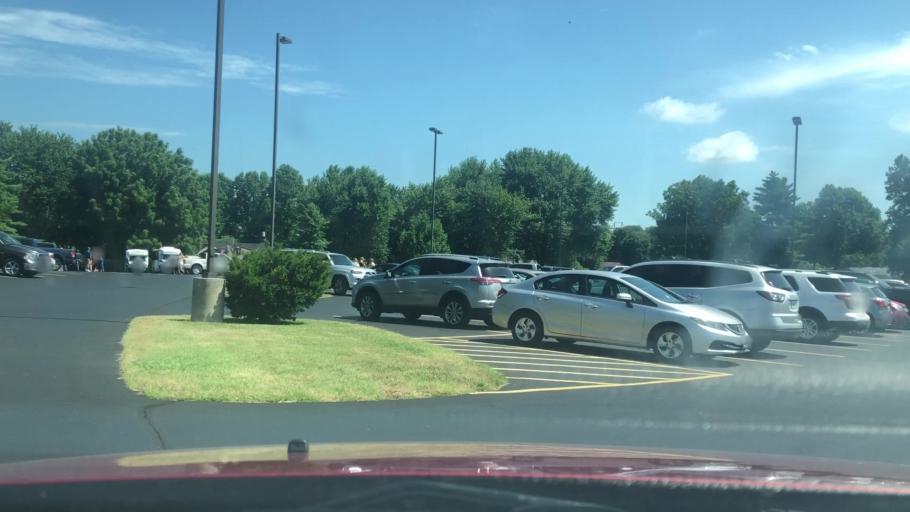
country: US
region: Missouri
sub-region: Greene County
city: Springfield
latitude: 37.2843
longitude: -93.2633
